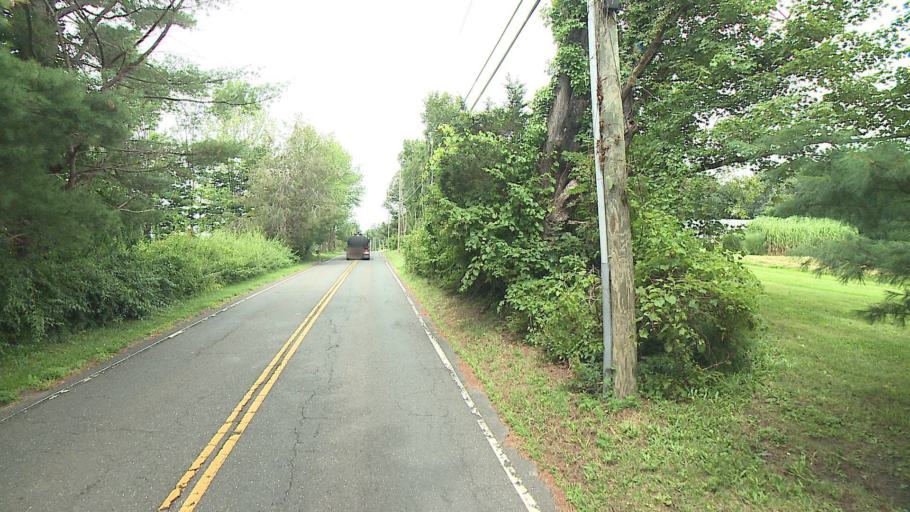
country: US
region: Connecticut
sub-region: Litchfield County
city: New Milford
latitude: 41.5140
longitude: -73.3606
